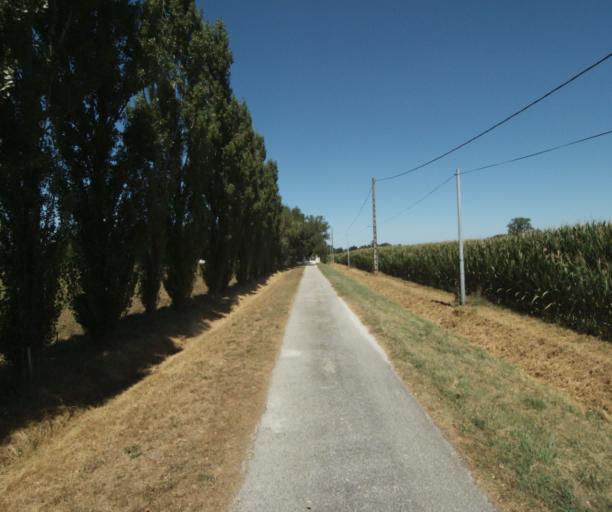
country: FR
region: Midi-Pyrenees
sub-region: Departement de la Haute-Garonne
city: Revel
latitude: 43.4751
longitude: 1.9517
